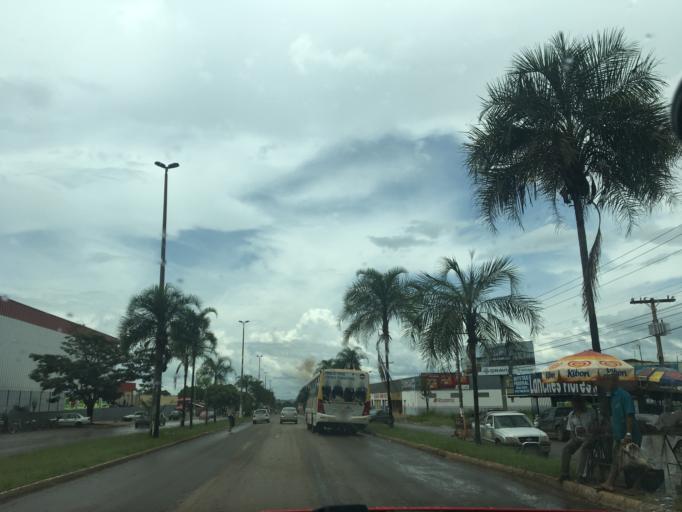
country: BR
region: Goias
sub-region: Luziania
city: Luziania
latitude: -16.2458
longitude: -47.9095
